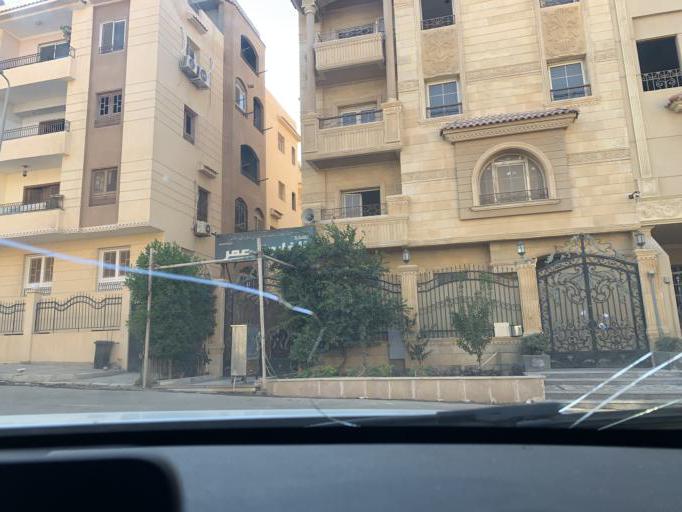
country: EG
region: Muhafazat al Qalyubiyah
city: Al Khankah
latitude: 30.0025
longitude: 31.4814
